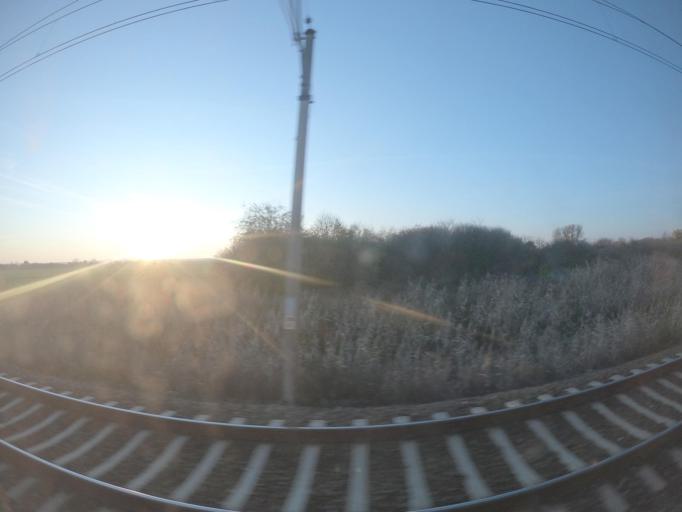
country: PL
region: Lubusz
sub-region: Powiat slubicki
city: Gorzyca
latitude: 52.5335
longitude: 14.6507
